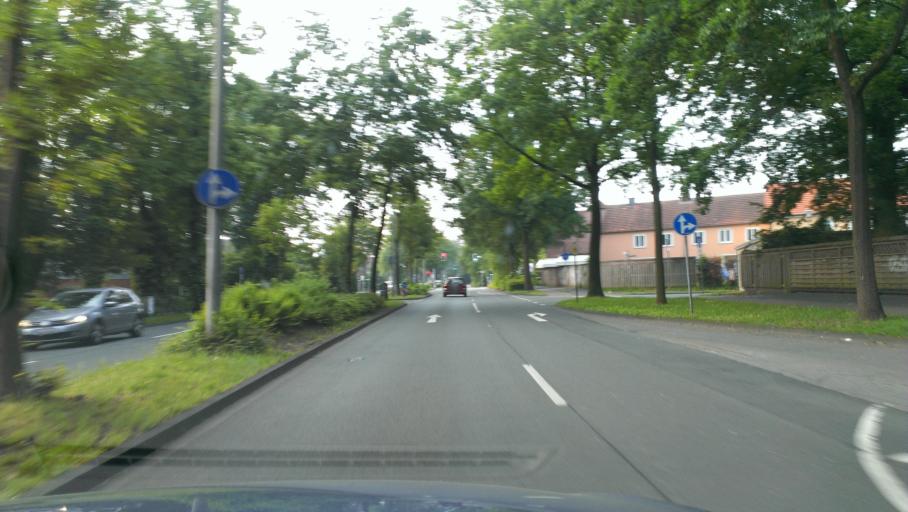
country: DE
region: North Rhine-Westphalia
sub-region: Regierungsbezirk Munster
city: Muenster
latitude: 51.9252
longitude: 7.6711
